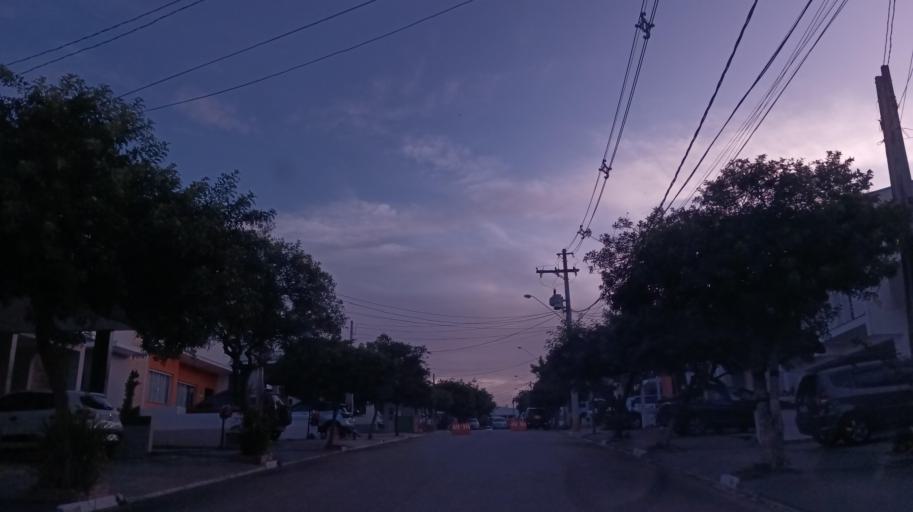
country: BR
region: Sao Paulo
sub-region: Sorocaba
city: Sorocaba
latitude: -23.4418
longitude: -47.4943
